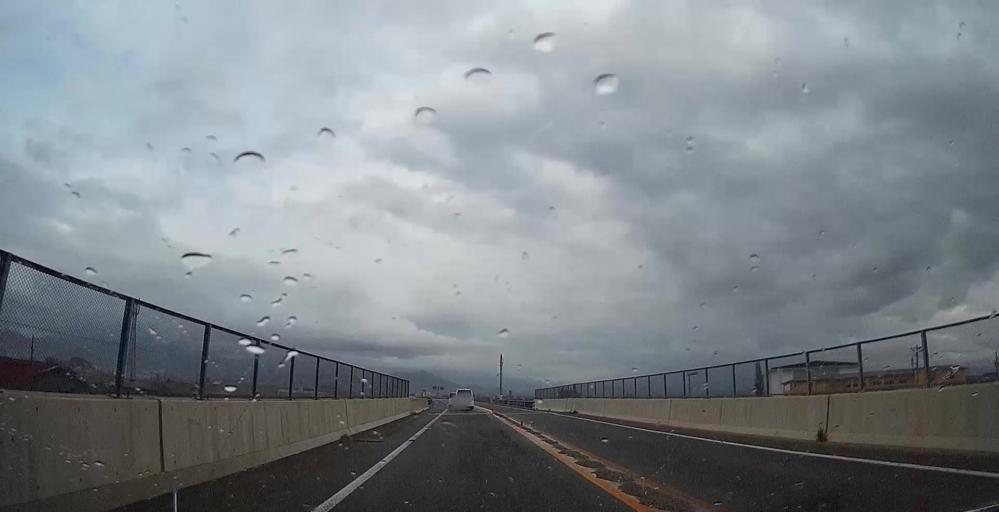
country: JP
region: Yamagata
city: Takahata
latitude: 38.0418
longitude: 140.1393
